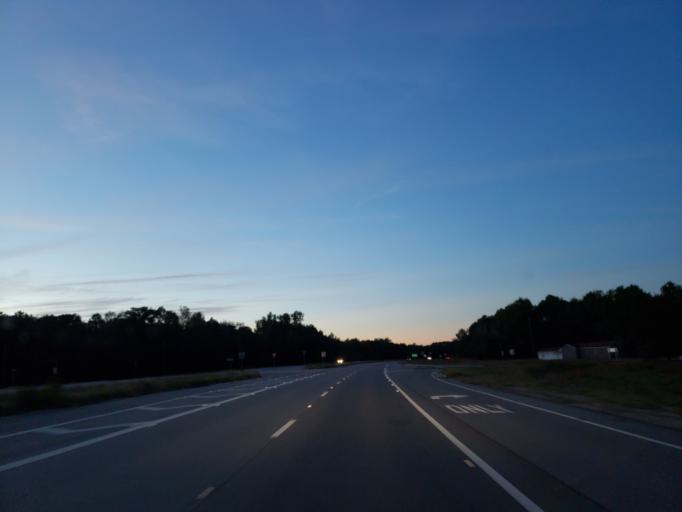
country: US
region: Mississippi
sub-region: Wayne County
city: Waynesboro
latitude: 31.8496
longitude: -88.7168
